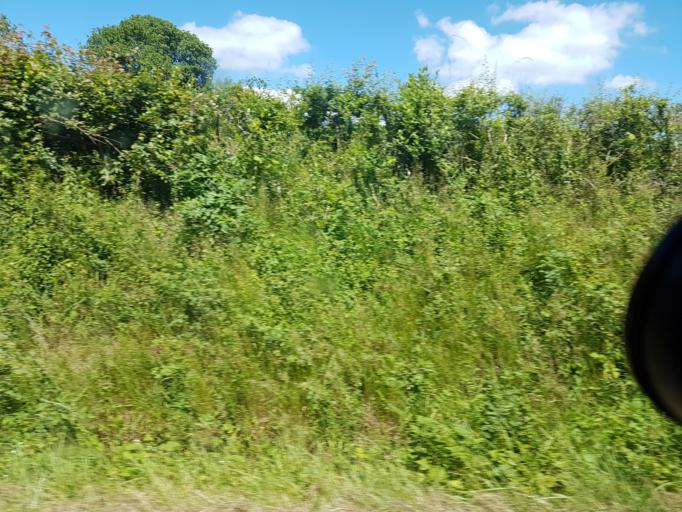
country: FR
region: Bourgogne
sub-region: Departement de Saone-et-Loire
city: Autun
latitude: 47.0585
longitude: 4.2667
